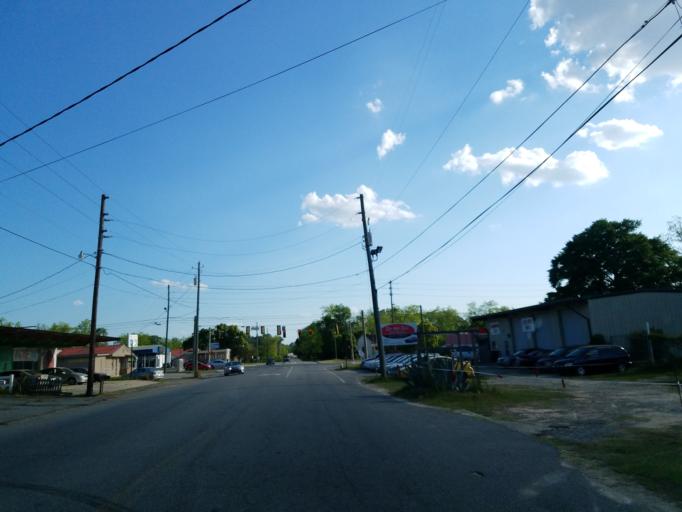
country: US
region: Georgia
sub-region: Tift County
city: Tifton
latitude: 31.4516
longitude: -83.5162
